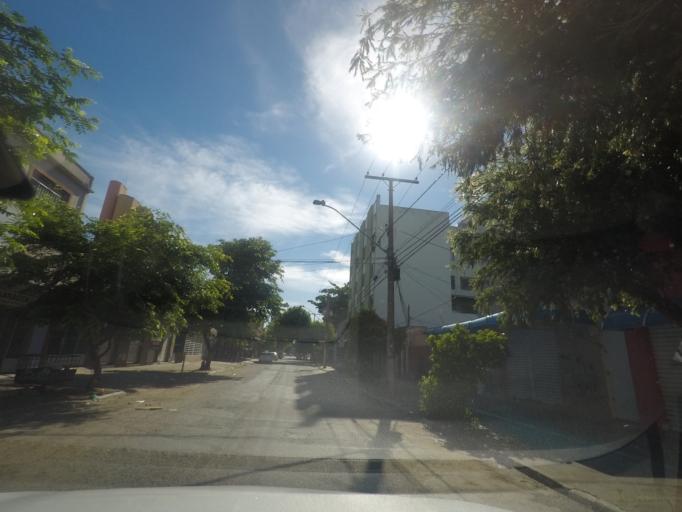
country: BR
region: Goias
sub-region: Goiania
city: Goiania
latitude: -16.6691
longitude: -49.2618
